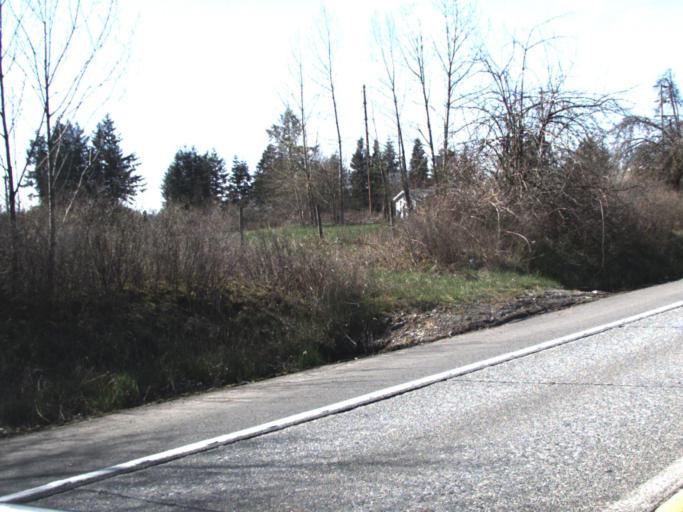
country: US
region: Washington
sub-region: Pierce County
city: Buckley
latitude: 47.2251
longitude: -122.1000
